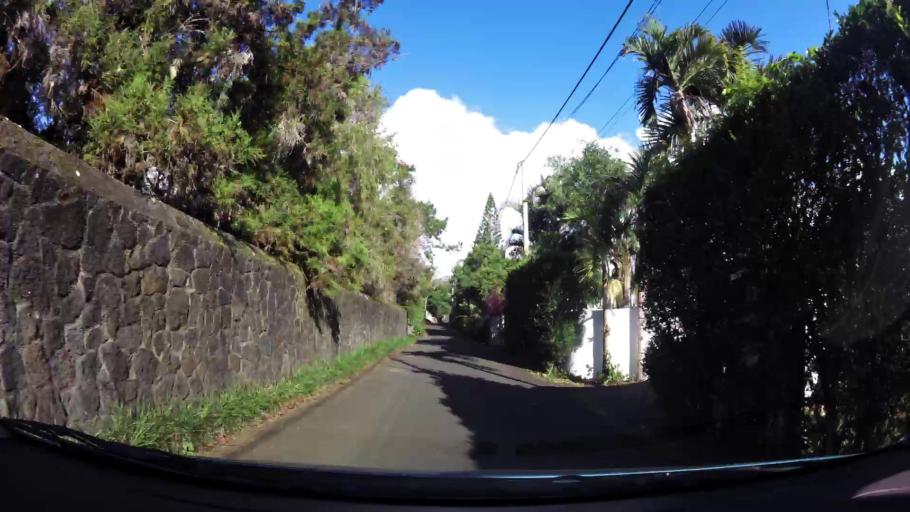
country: MU
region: Plaines Wilhems
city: Curepipe
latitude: -20.3117
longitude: 57.5021
